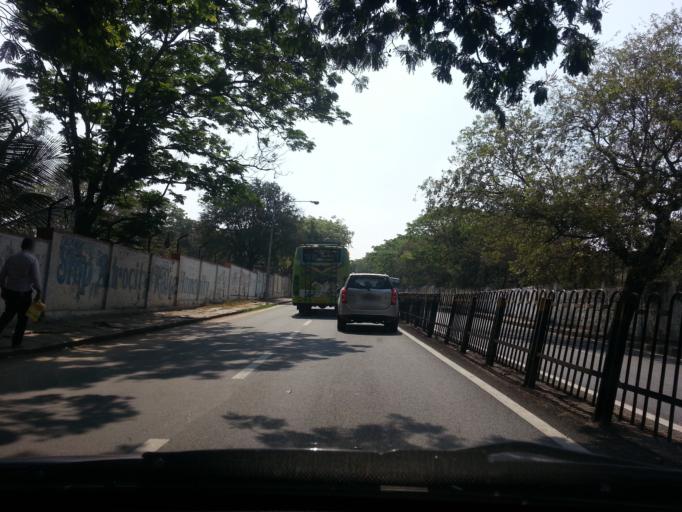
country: IN
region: Karnataka
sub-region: Mysore
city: Mysore
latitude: 12.3249
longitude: 76.6589
